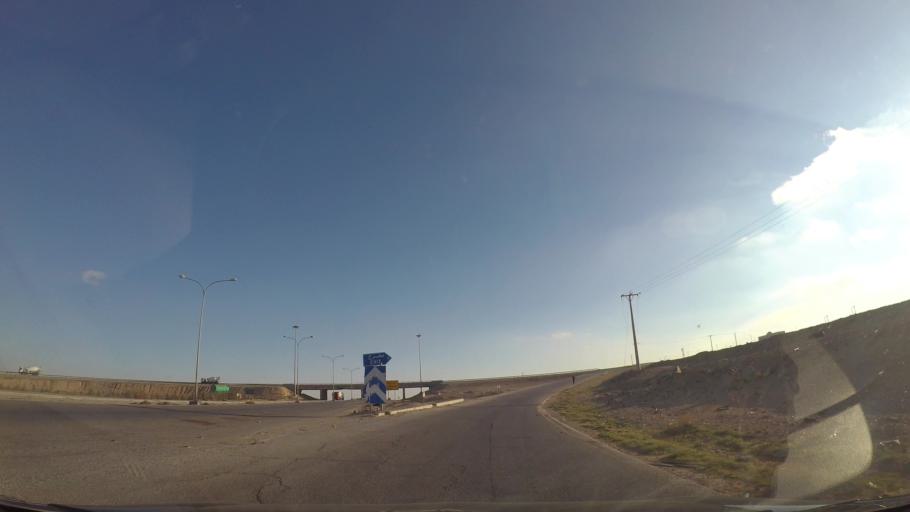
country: JO
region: Tafielah
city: Busayra
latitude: 30.5002
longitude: 35.7993
